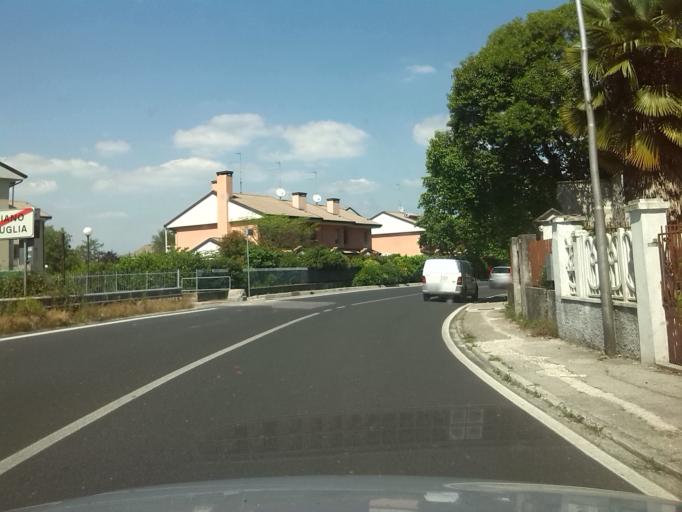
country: IT
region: Friuli Venezia Giulia
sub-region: Provincia di Gorizia
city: Fogliano
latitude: 45.8703
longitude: 13.4806
